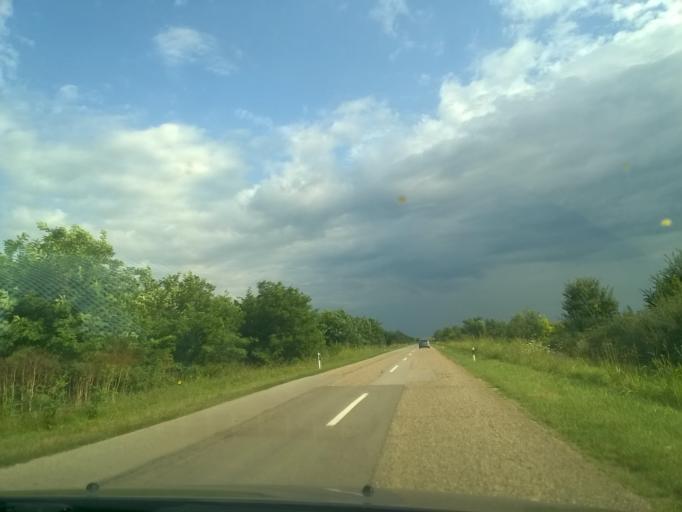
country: RS
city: Uzdin
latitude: 45.1772
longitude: 20.6180
